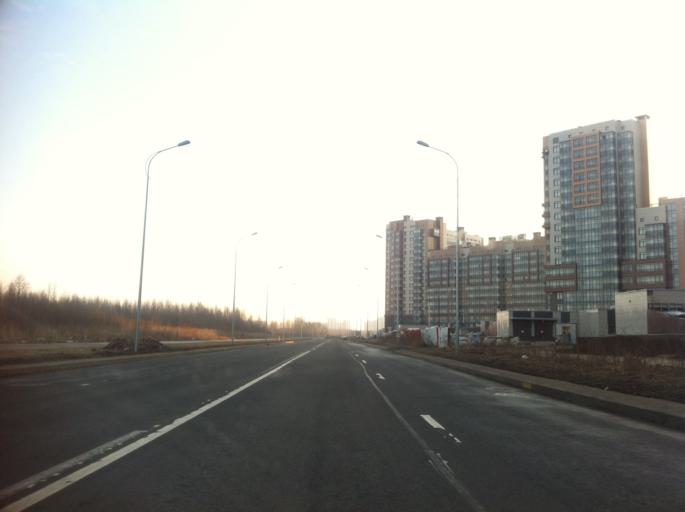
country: RU
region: St.-Petersburg
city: Sosnovaya Polyana
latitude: 59.8518
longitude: 30.1358
